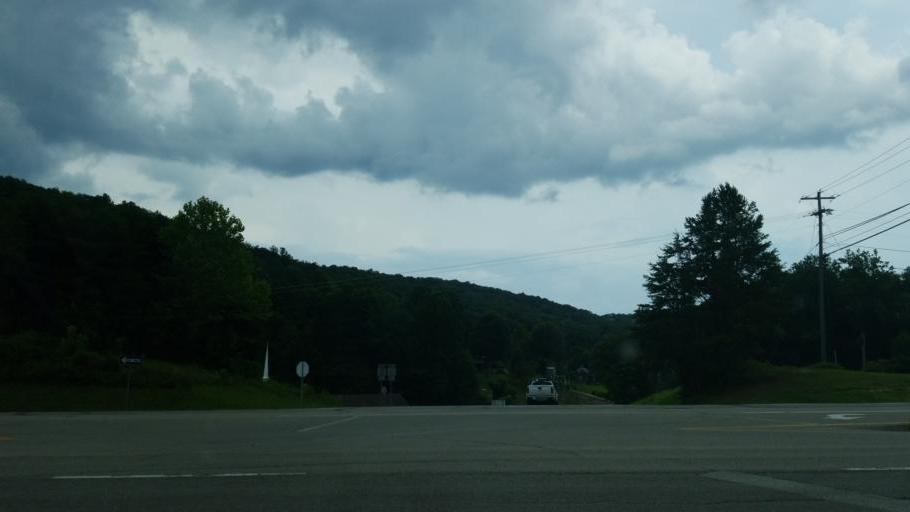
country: US
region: West Virginia
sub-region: Kanawha County
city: Alum Creek
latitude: 38.2783
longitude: -81.7751
